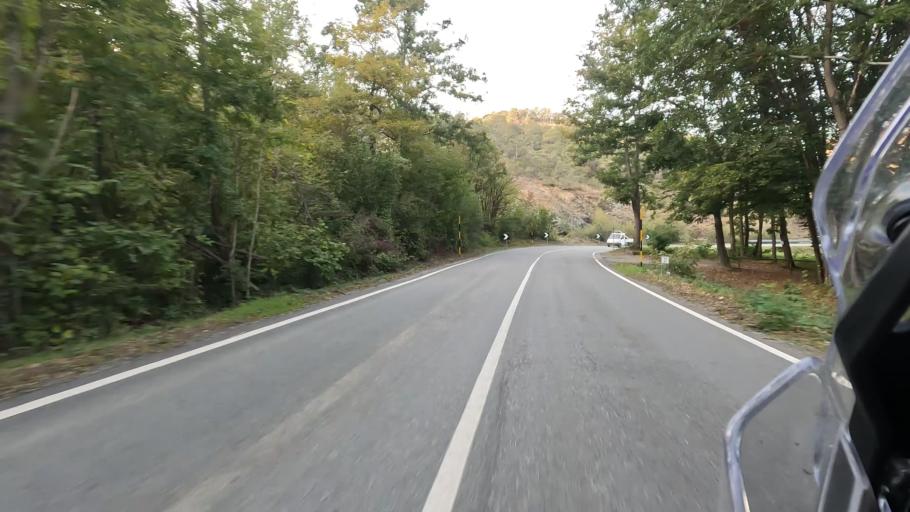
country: IT
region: Liguria
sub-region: Provincia di Savona
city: Sassello
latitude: 44.5153
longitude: 8.4728
